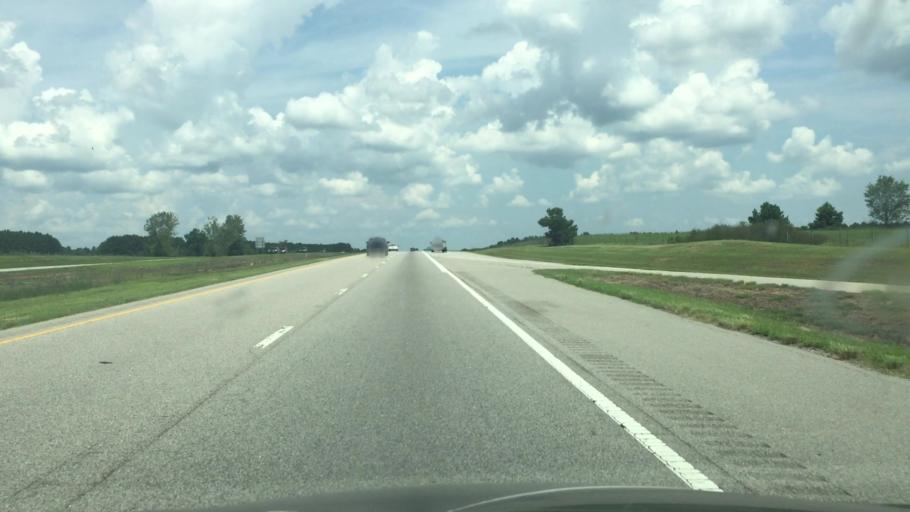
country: US
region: North Carolina
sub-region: Richmond County
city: Ellerbe
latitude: 35.1494
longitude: -79.7144
